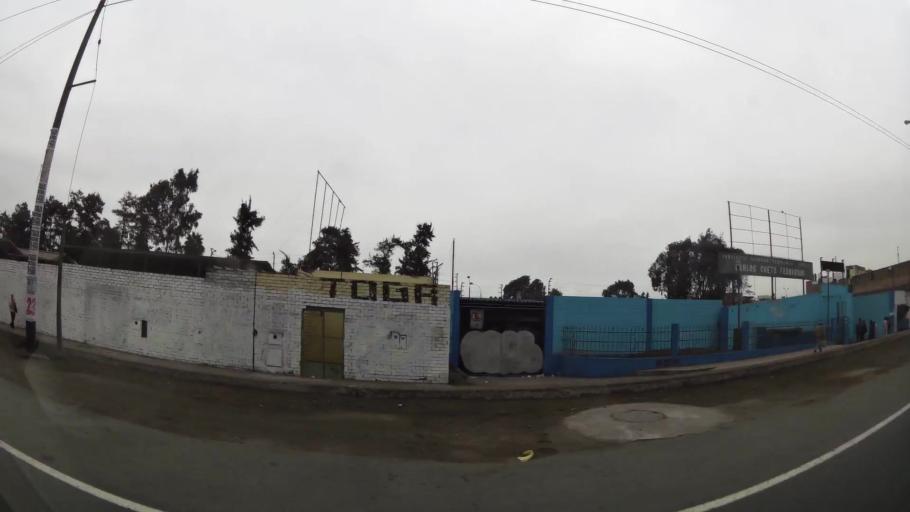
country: PE
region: Lima
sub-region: Lima
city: Independencia
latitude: -11.9634
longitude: -77.0550
